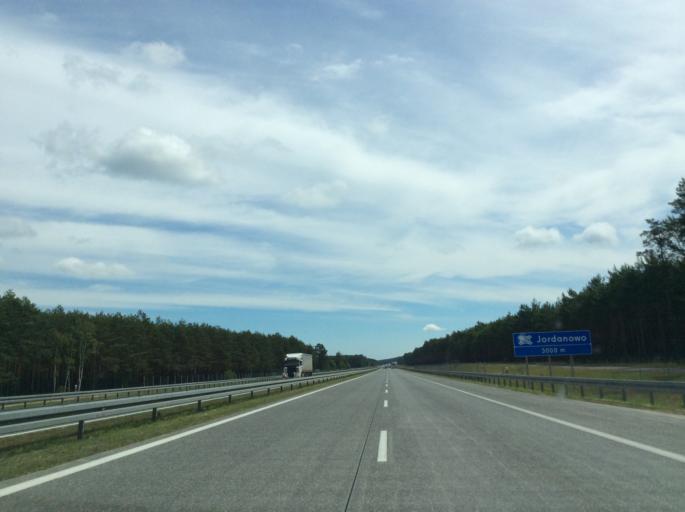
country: PL
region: Lubusz
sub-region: Powiat swiebodzinski
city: Lubrza
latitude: 52.3191
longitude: 15.4932
